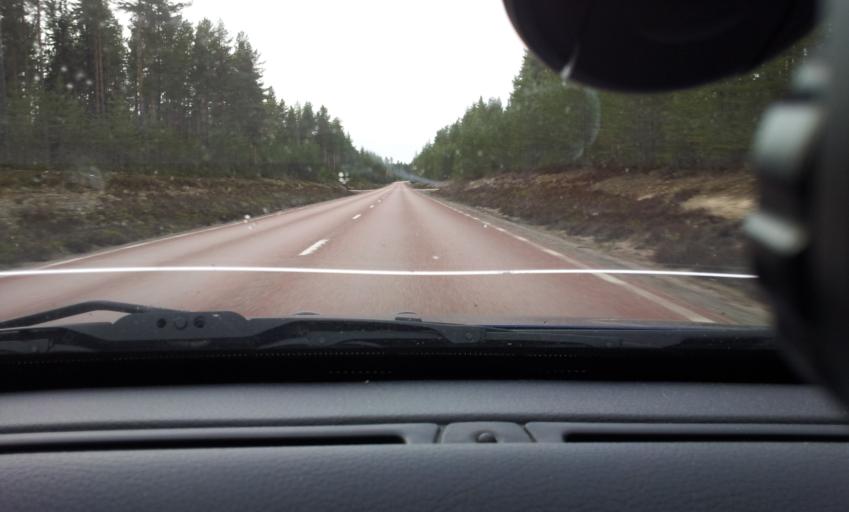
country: SE
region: Gaevleborg
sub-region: Ljusdals Kommun
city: Farila
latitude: 61.8111
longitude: 15.7702
